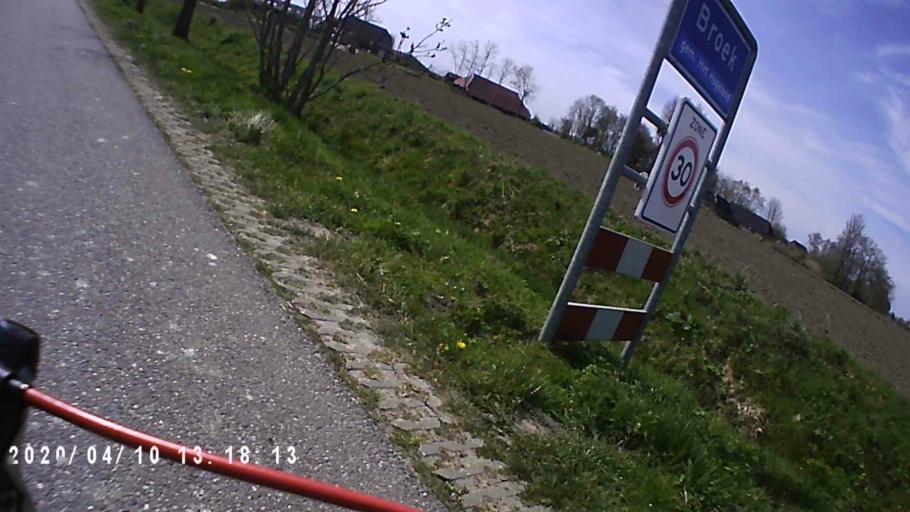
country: NL
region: Groningen
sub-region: Gemeente Zuidhorn
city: Oldehove
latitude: 53.3949
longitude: 6.4244
